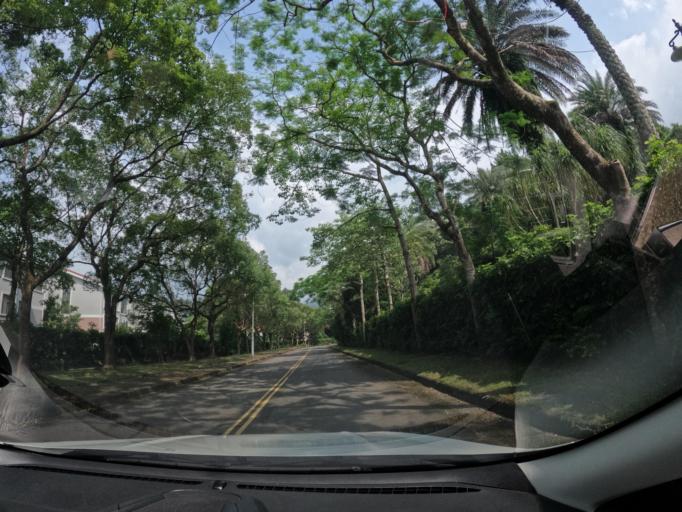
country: TW
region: Taiwan
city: Daxi
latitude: 24.8869
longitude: 121.3227
